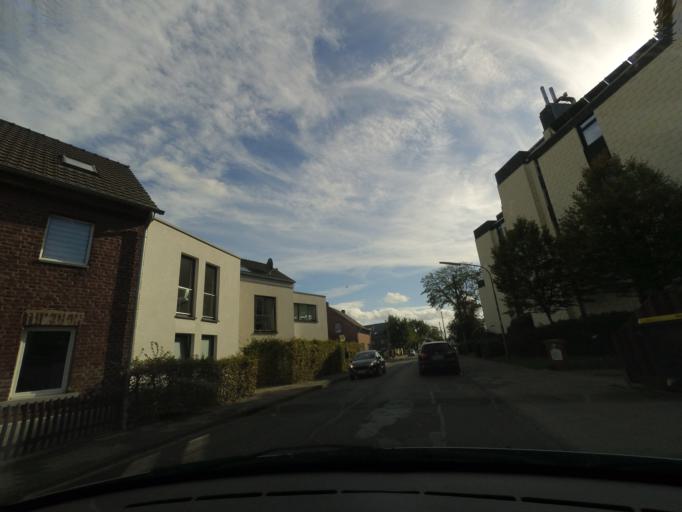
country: DE
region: North Rhine-Westphalia
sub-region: Regierungsbezirk Dusseldorf
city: Korschenbroich
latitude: 51.1901
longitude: 6.5609
